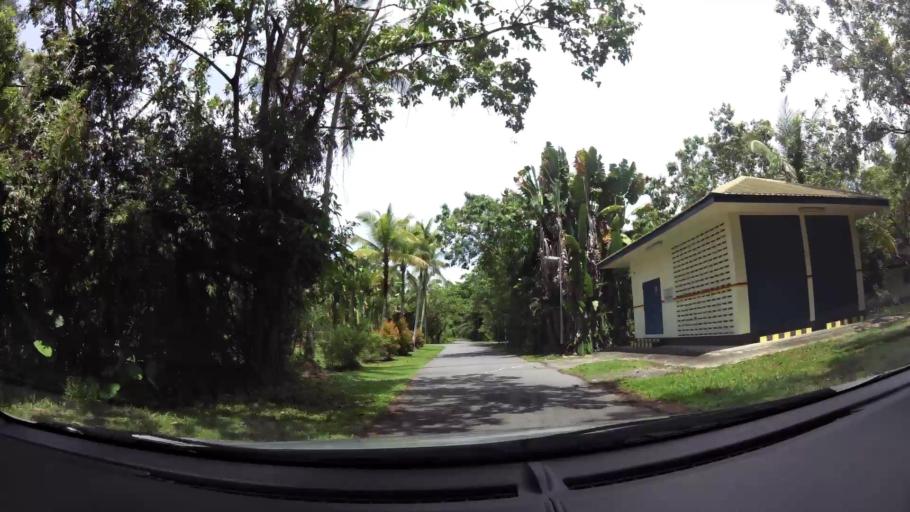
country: BN
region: Belait
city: Kuala Belait
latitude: 4.5948
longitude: 114.2582
